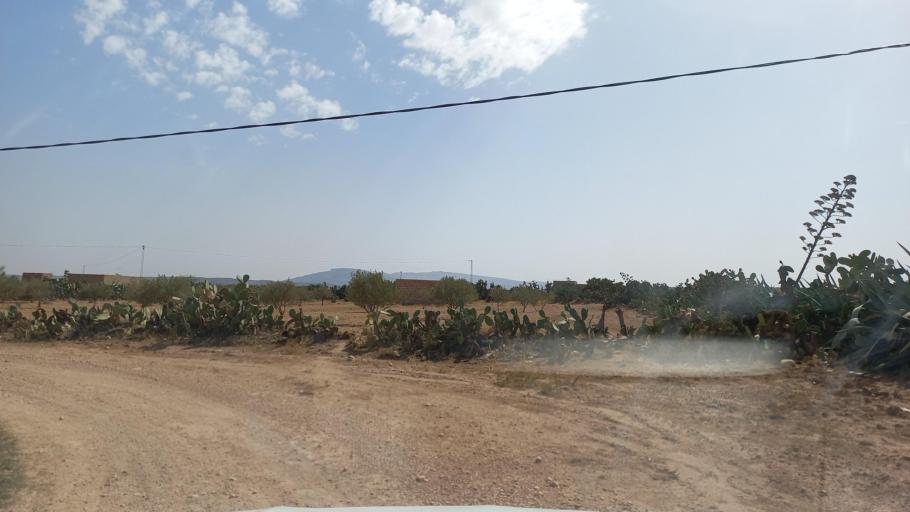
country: TN
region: Al Qasrayn
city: Kasserine
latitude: 35.2785
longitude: 8.9683
